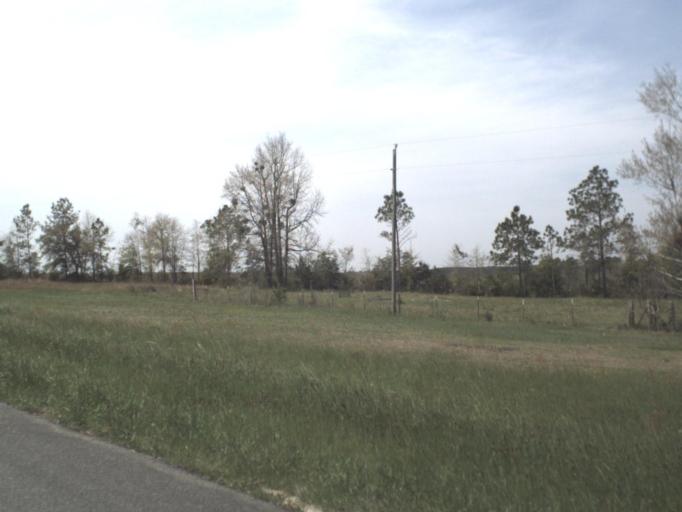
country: US
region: Florida
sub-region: Walton County
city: DeFuniak Springs
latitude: 30.7247
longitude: -85.9770
